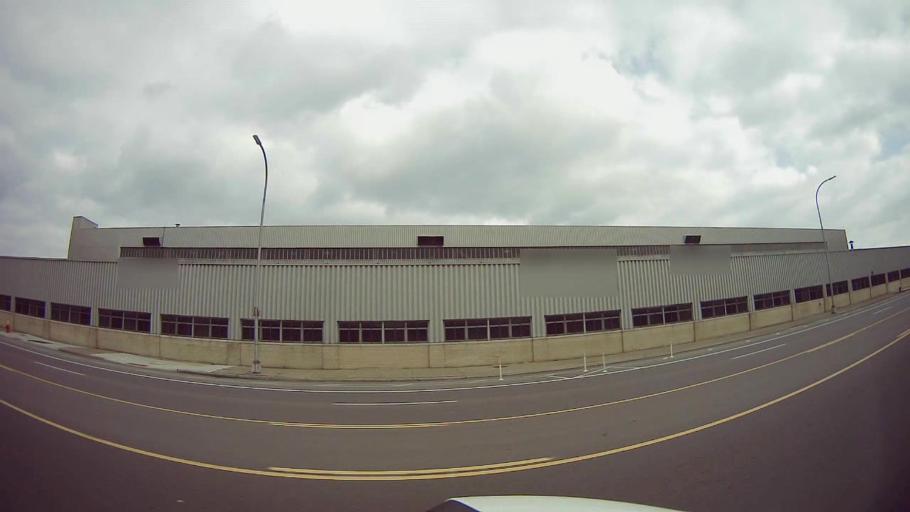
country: US
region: Michigan
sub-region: Wayne County
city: Dearborn
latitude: 42.3504
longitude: -83.1347
